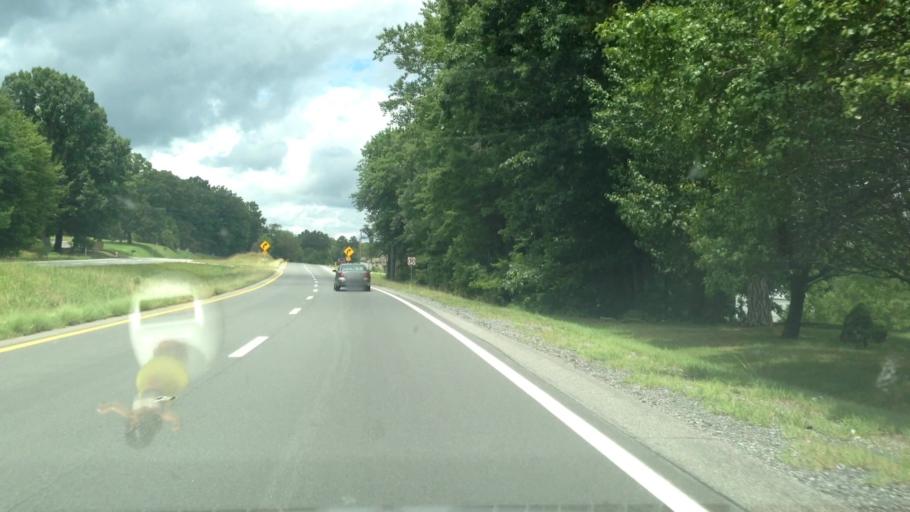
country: US
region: Virginia
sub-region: Henry County
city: Stanleytown
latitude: 36.8055
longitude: -79.9376
